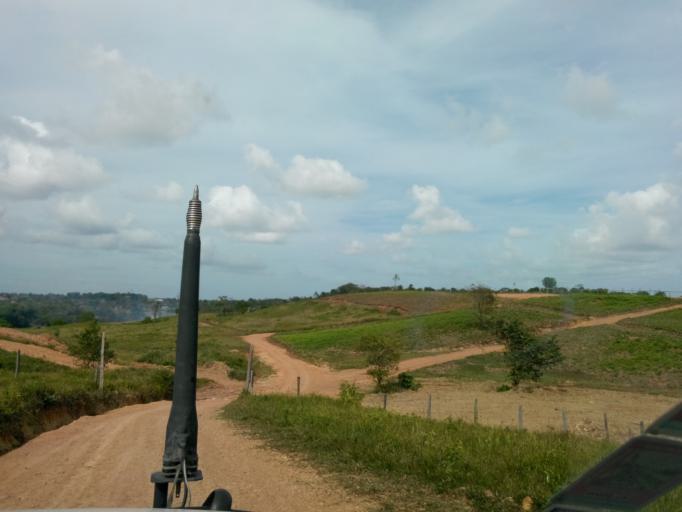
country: NI
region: Atlantico Sur
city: Bluefields
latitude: 11.9953
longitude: -83.7744
